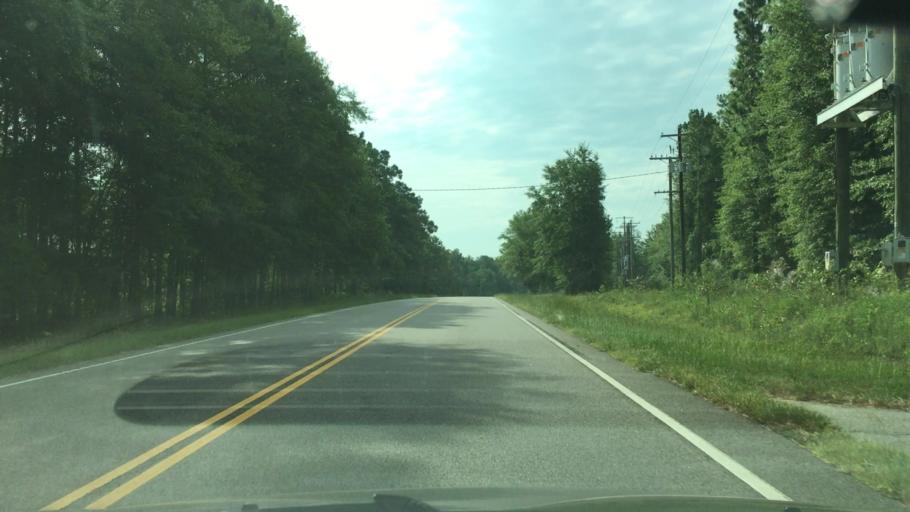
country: US
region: South Carolina
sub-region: Barnwell County
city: Williston
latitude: 33.6584
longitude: -81.3809
